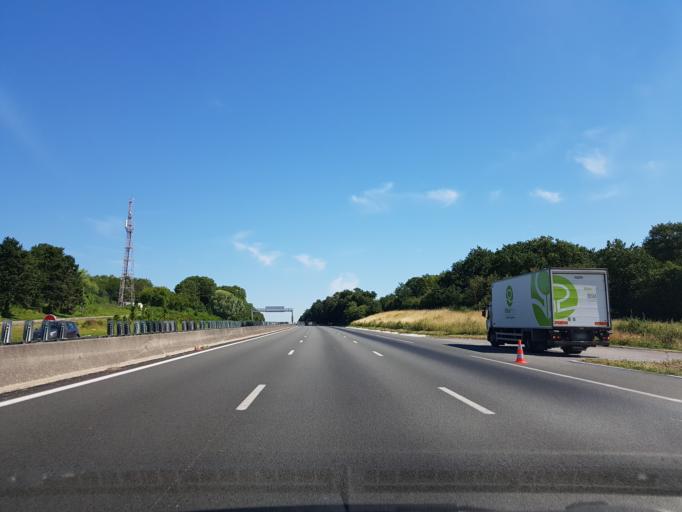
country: FR
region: Picardie
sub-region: Departement de l'Oise
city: Longueil-Sainte-Marie
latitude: 49.3506
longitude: 2.7009
